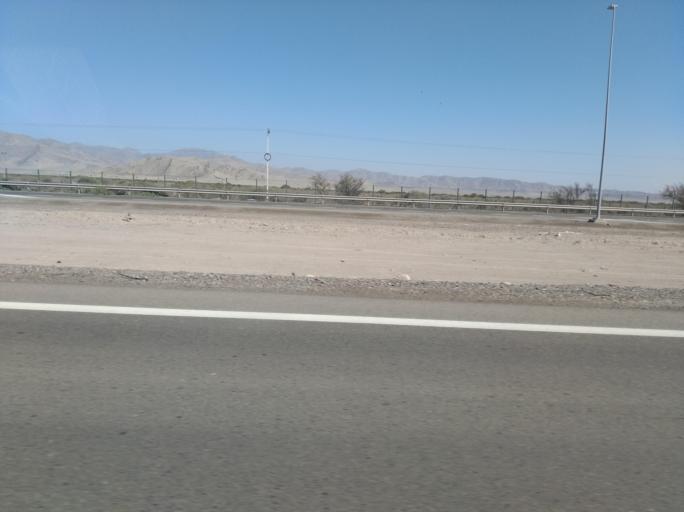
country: CL
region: Atacama
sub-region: Provincia de Copiapo
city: Copiapo
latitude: -27.3420
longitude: -70.6139
